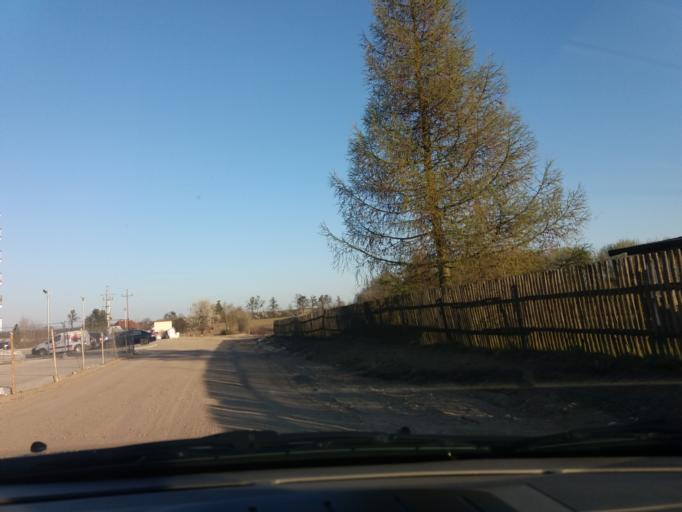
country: PL
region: Warmian-Masurian Voivodeship
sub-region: Powiat szczycienski
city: Szczytno
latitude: 53.5529
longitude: 20.9832
